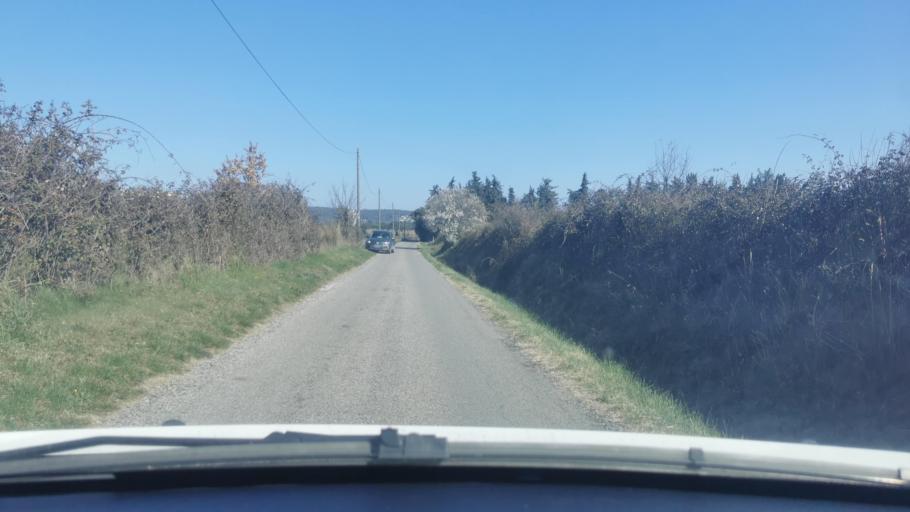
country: FR
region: Languedoc-Roussillon
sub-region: Departement du Gard
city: Montaren-et-Saint-Mediers
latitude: 44.0373
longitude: 4.3896
